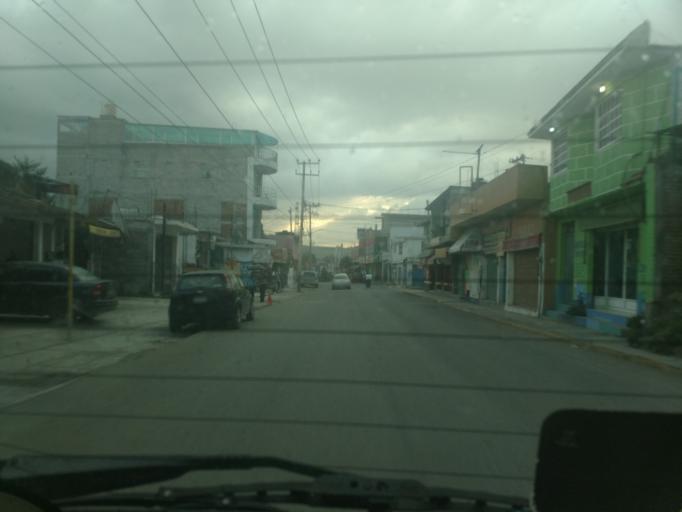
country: MX
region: Morelos
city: Coyotepec
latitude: 19.7773
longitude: -99.2159
